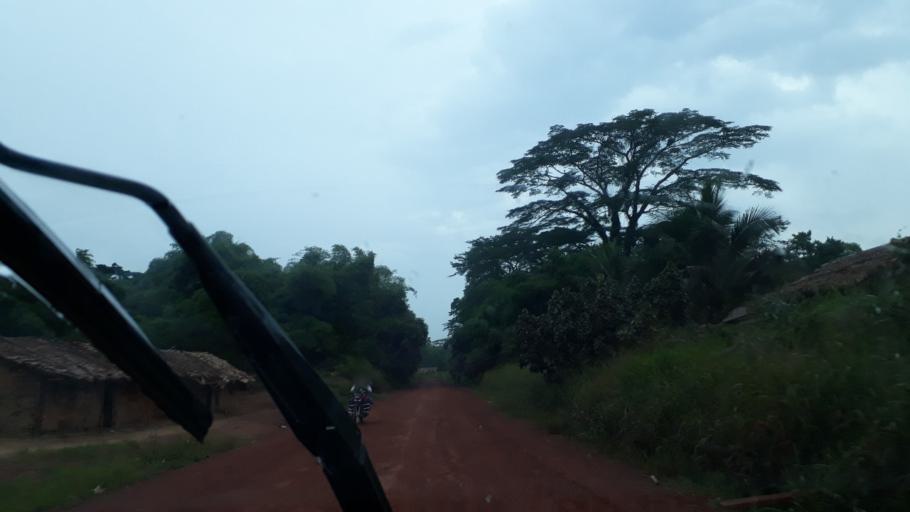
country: CD
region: Eastern Province
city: Kisangani
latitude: 0.4643
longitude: 25.4616
